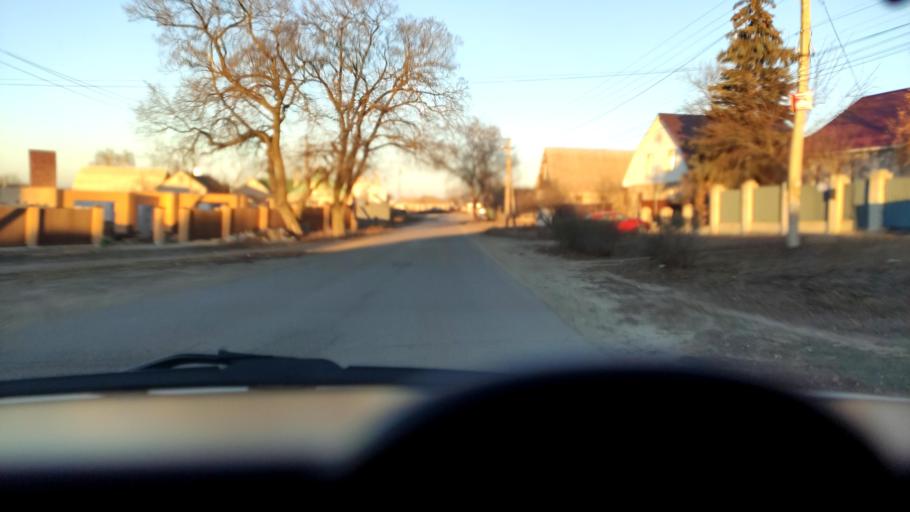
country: RU
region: Voronezj
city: Podgornoye
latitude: 51.7399
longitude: 39.1490
